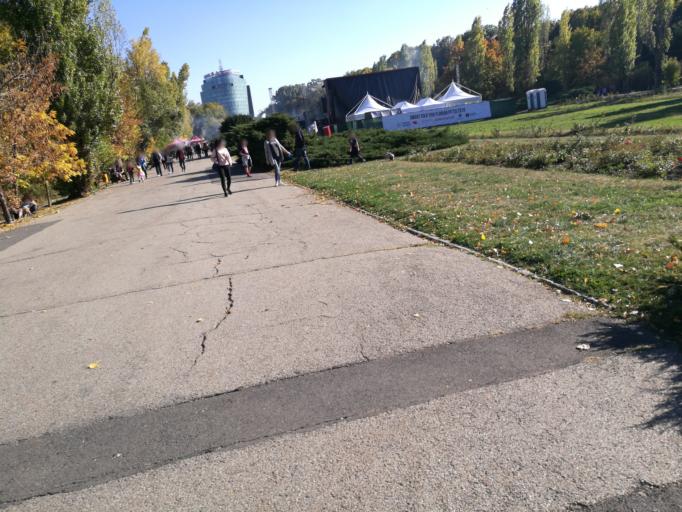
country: RO
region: Bucuresti
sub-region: Municipiul Bucuresti
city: Bucuresti
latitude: 44.4700
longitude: 26.0834
